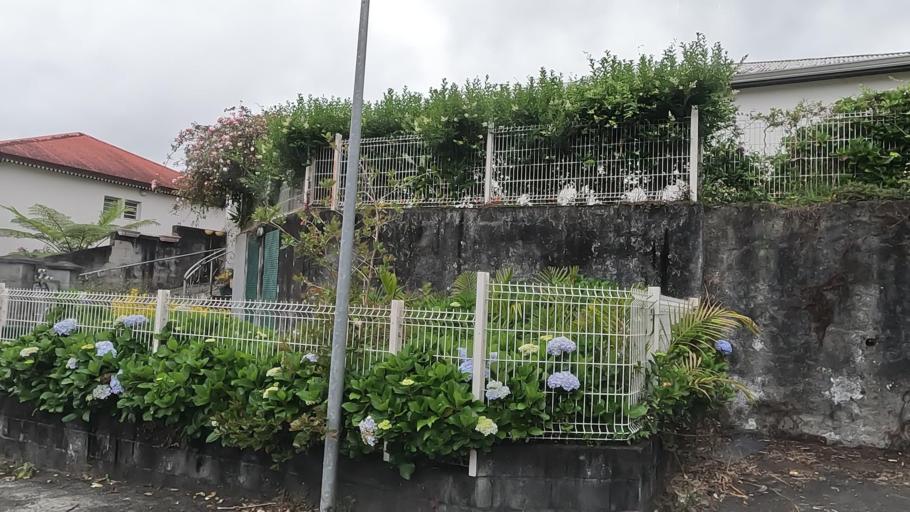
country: RE
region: Reunion
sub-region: Reunion
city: Saint-Benoit
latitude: -21.1409
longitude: 55.6253
